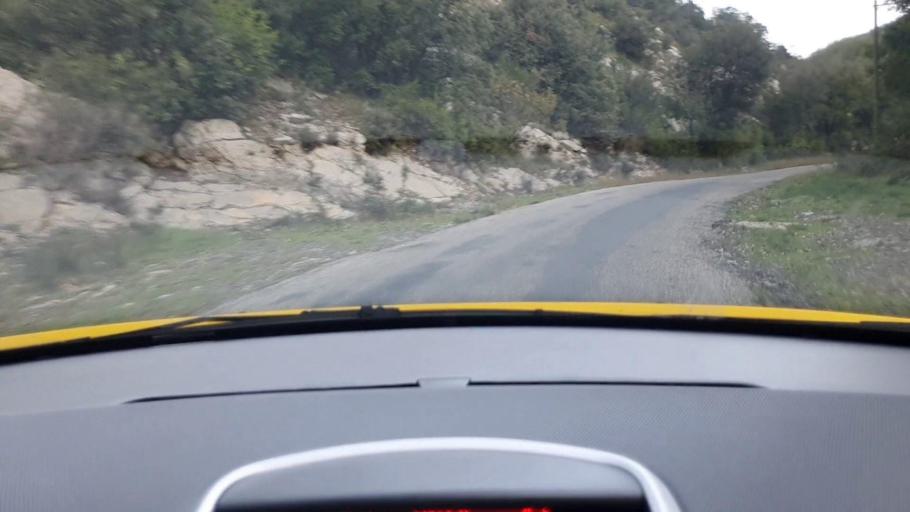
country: FR
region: Languedoc-Roussillon
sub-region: Departement du Gard
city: Saint-Hippolyte-du-Fort
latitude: 43.9632
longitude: 3.8077
